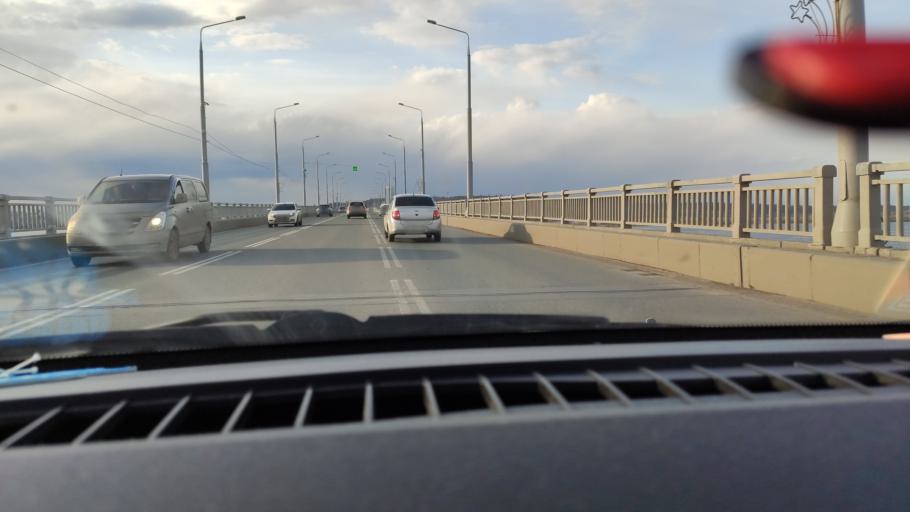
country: RU
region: Saratov
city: Engel's
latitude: 51.5102
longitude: 46.0750
